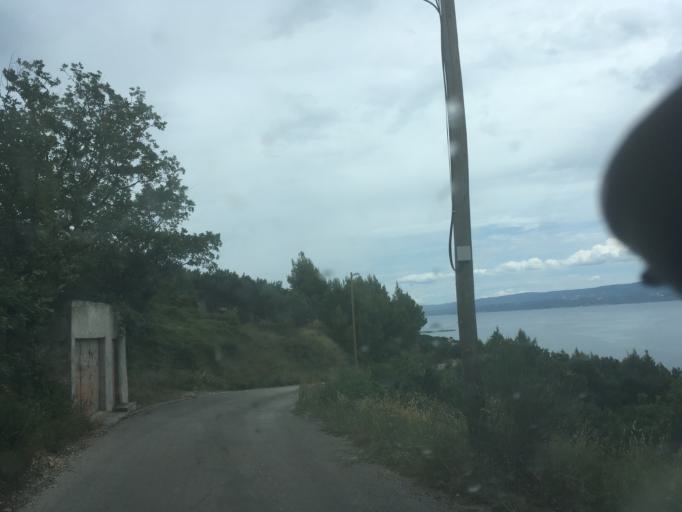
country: HR
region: Splitsko-Dalmatinska
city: Jesenice
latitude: 43.4592
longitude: 16.6168
